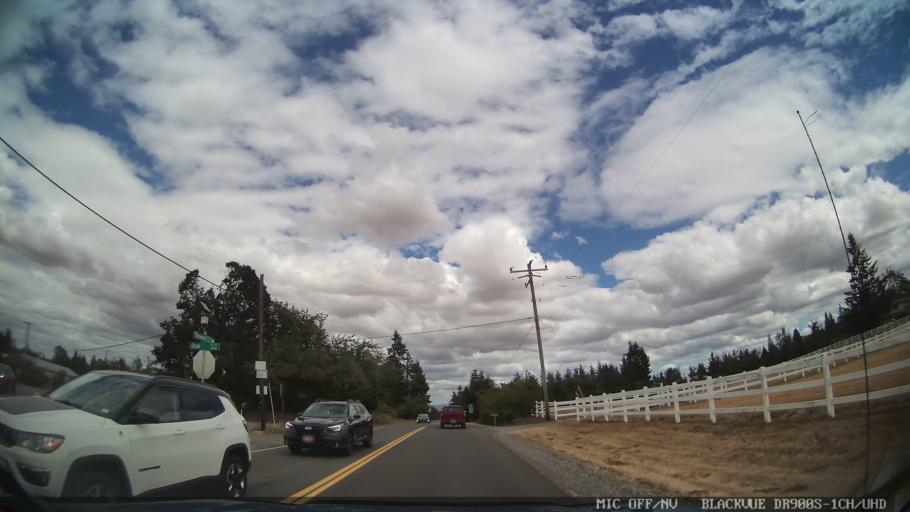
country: US
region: Oregon
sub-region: Marion County
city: Aumsville
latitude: 44.8604
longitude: -122.8615
